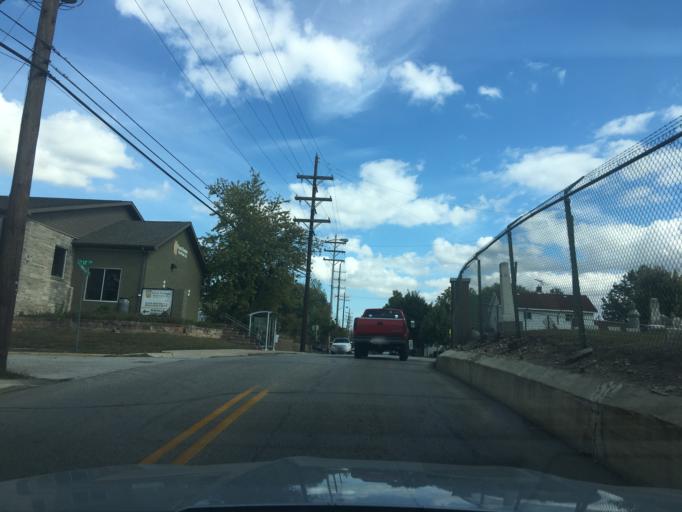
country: US
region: Indiana
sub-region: Tippecanoe County
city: Lafayette
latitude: 40.4321
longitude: -86.8849
